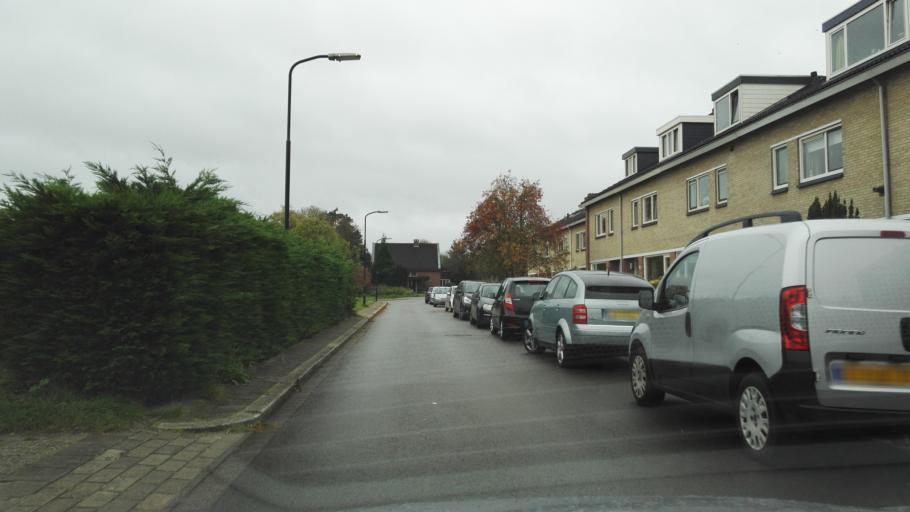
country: NL
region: Gelderland
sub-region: Gemeente Apeldoorn
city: Apeldoorn
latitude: 52.2316
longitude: 5.9955
